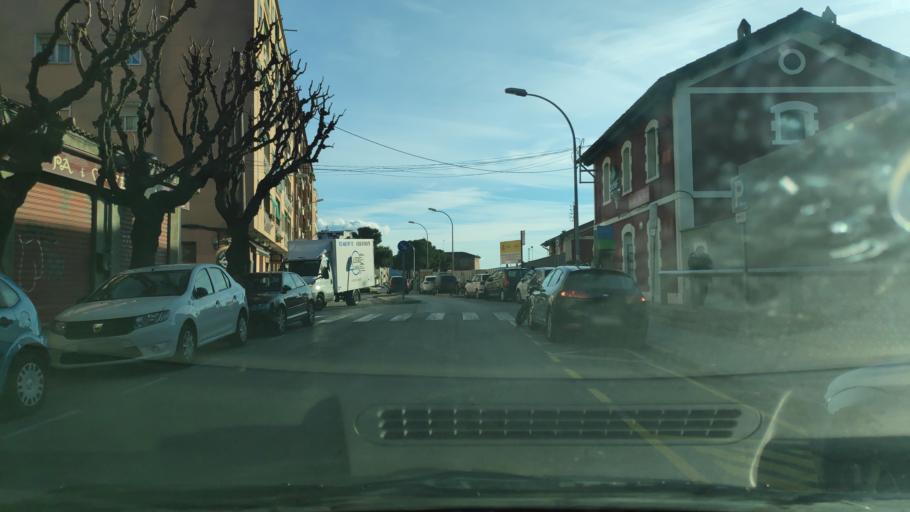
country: ES
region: Catalonia
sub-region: Provincia de Barcelona
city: Mollet del Valles
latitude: 41.5369
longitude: 2.2063
